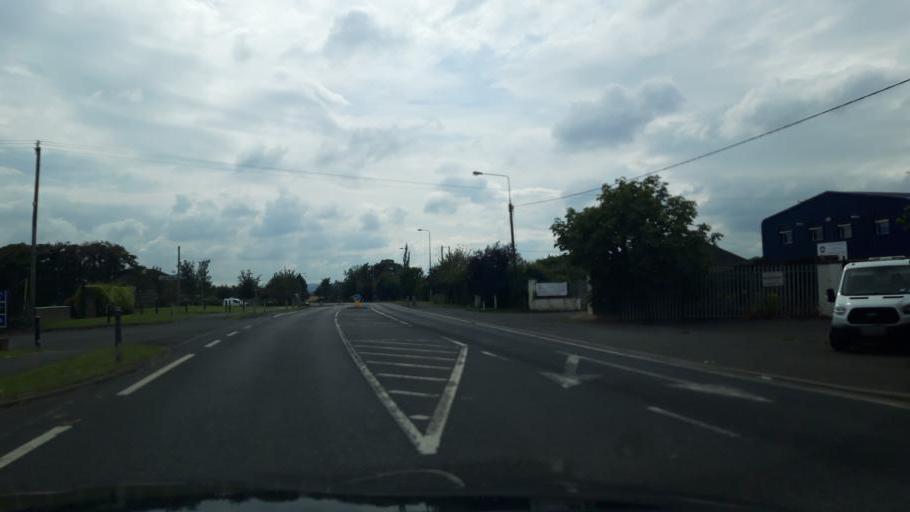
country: IE
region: Leinster
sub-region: Kildare
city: Athy
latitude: 52.9863
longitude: -6.9978
